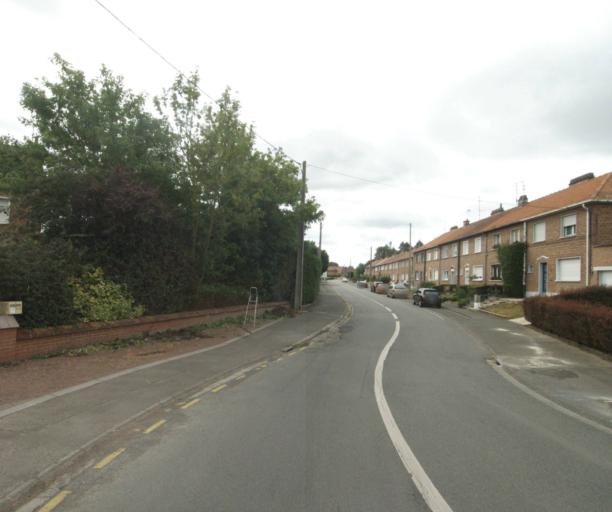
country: FR
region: Nord-Pas-de-Calais
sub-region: Departement du Nord
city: Linselles
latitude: 50.7446
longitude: 3.0845
